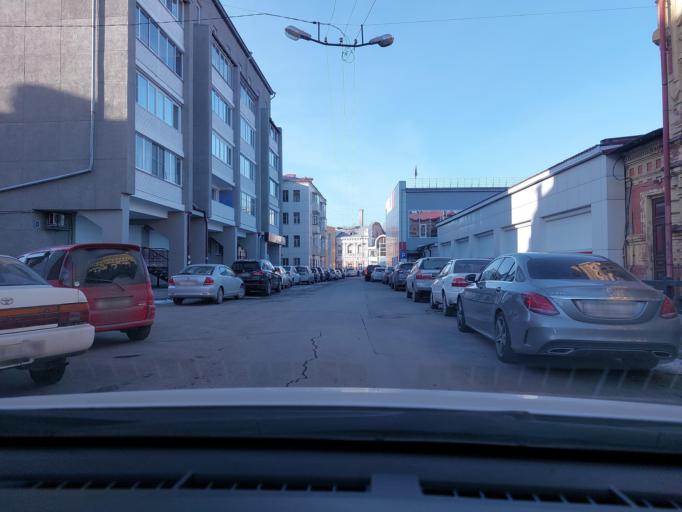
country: RU
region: Irkutsk
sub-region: Irkutskiy Rayon
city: Irkutsk
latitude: 52.2876
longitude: 104.2846
